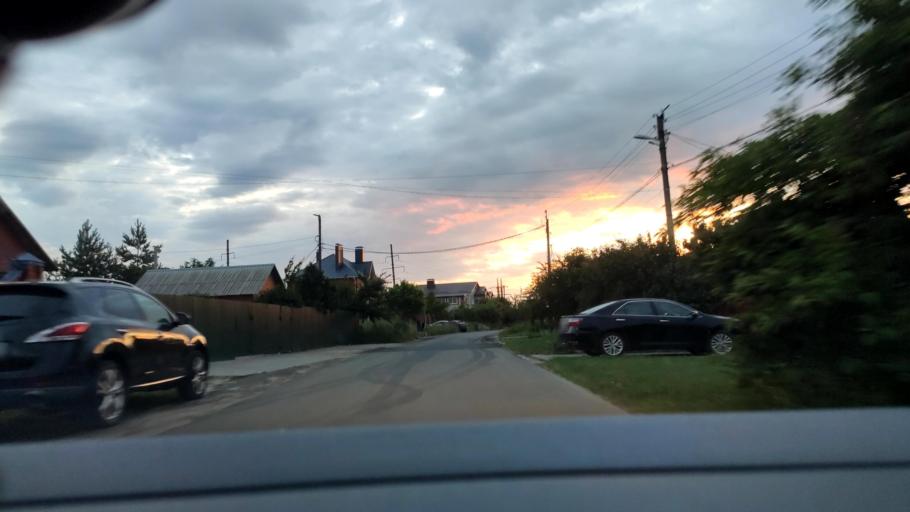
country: RU
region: Voronezj
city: Semiluki
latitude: 51.7040
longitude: 39.0242
